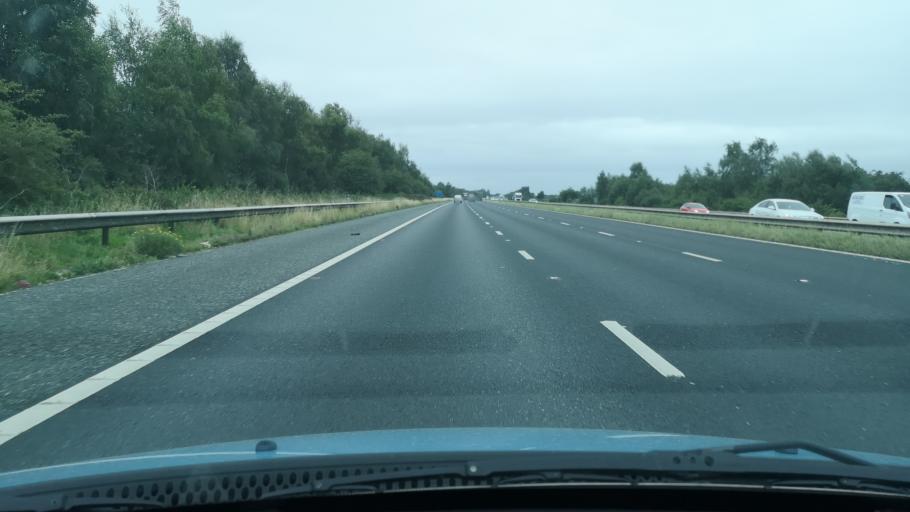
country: GB
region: England
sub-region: East Riding of Yorkshire
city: Pollington
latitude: 53.6832
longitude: -1.0750
